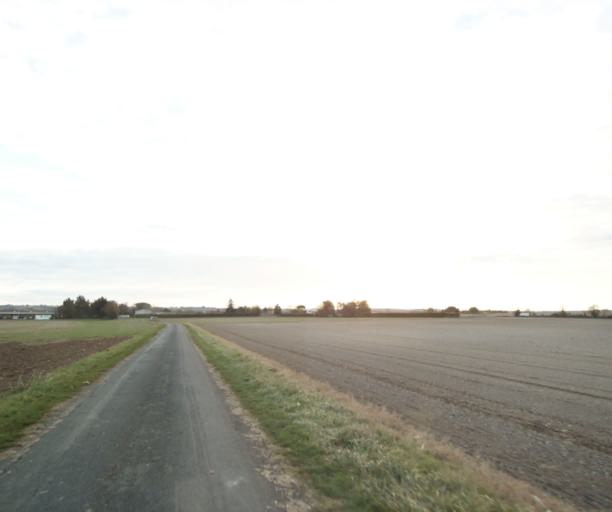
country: FR
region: Poitou-Charentes
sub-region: Departement de la Charente-Maritime
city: Les Gonds
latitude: 45.7009
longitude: -0.6174
